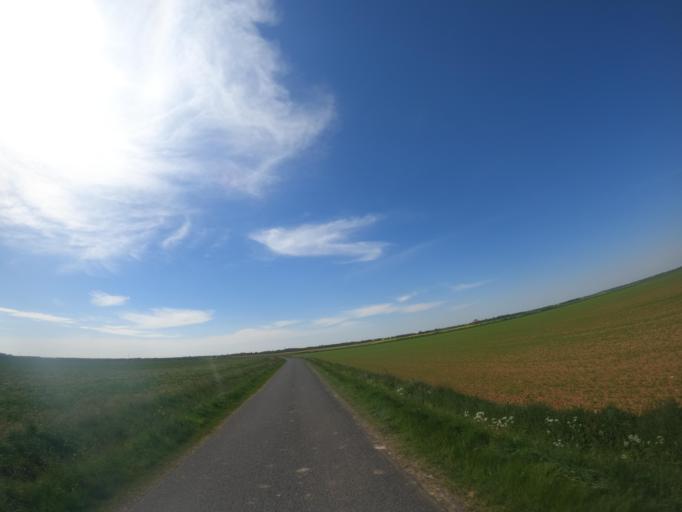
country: FR
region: Poitou-Charentes
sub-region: Departement des Deux-Sevres
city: Saint-Varent
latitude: 46.8994
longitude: -0.1740
